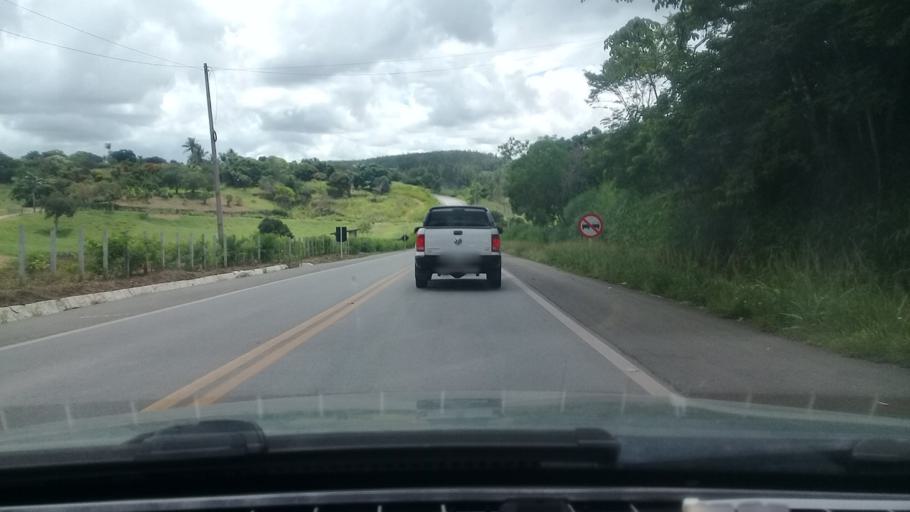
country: BR
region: Pernambuco
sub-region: Nazare Da Mata
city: Nazare da Mata
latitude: -7.7201
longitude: -35.2387
